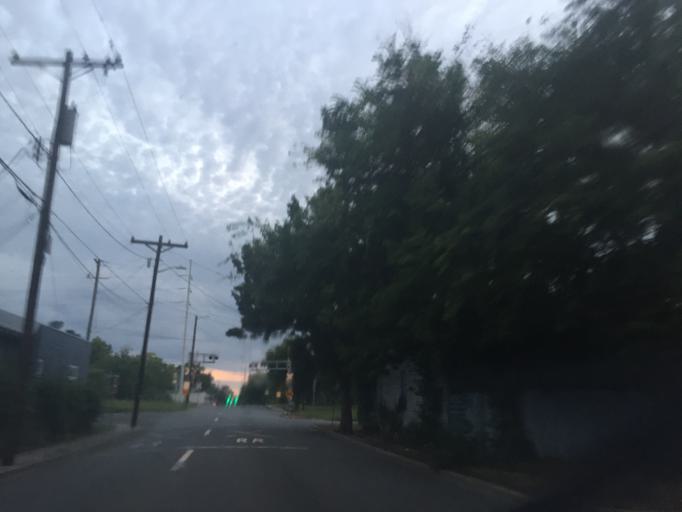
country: US
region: Georgia
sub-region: Chatham County
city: Savannah
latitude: 32.0579
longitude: -81.0918
